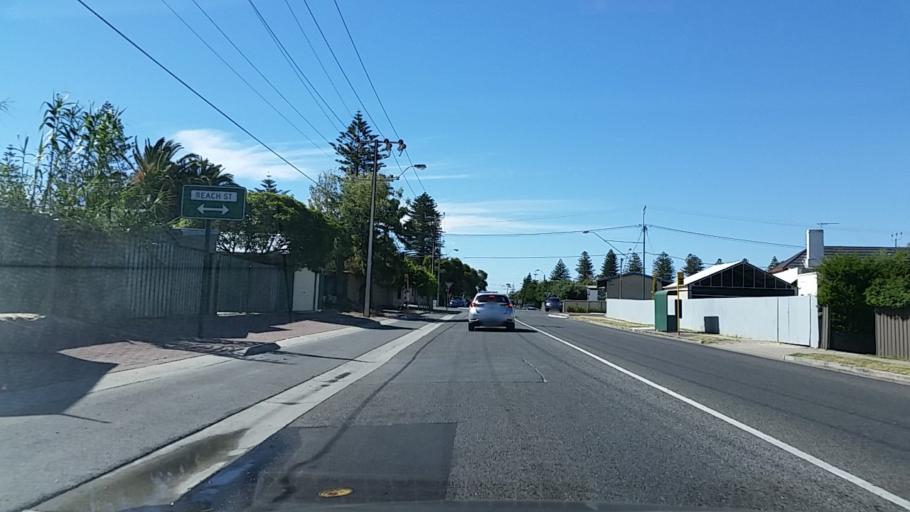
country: AU
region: South Australia
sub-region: Charles Sturt
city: Grange
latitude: -34.9059
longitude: 138.4916
